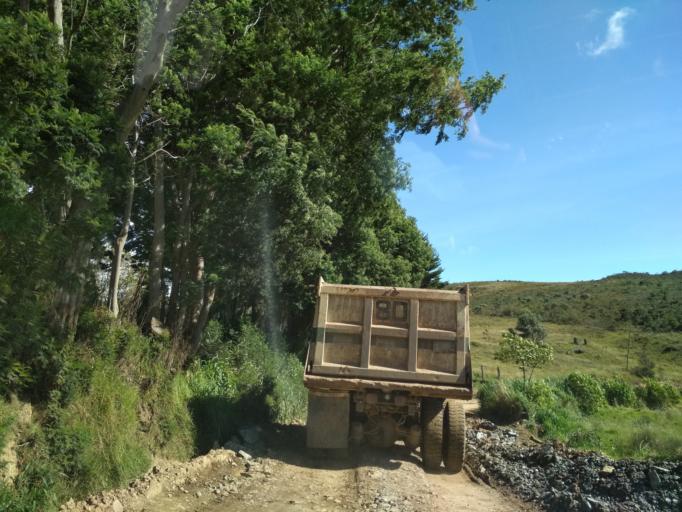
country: CO
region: Cauca
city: Silvia
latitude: 2.6934
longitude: -76.3320
